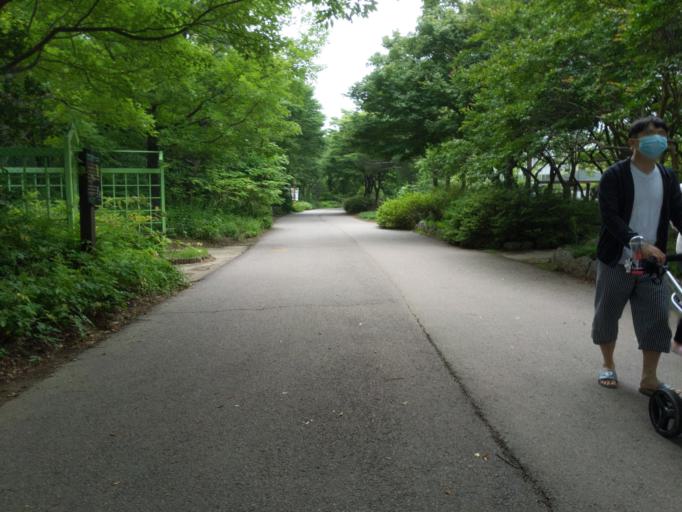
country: KR
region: Daegu
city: Hwawon
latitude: 35.7969
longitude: 128.5257
